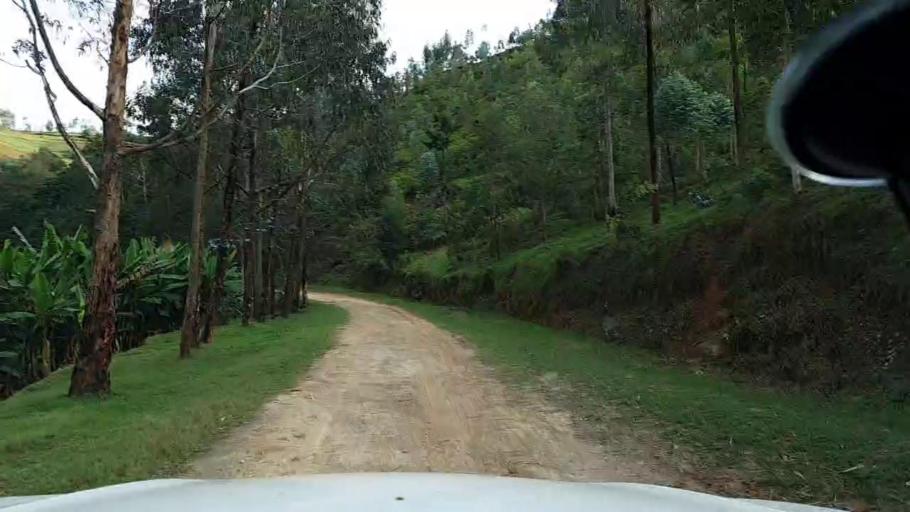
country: RW
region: Southern Province
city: Gitarama
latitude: -2.1629
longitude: 29.5494
